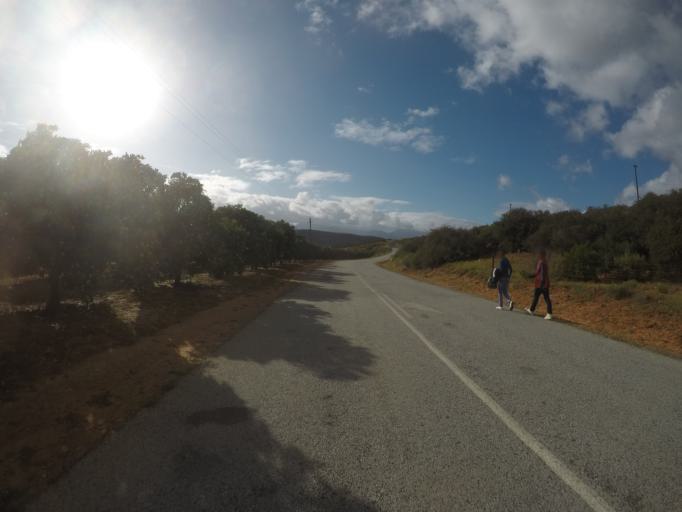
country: ZA
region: Western Cape
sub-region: West Coast District Municipality
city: Clanwilliam
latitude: -32.4199
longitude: 18.9299
